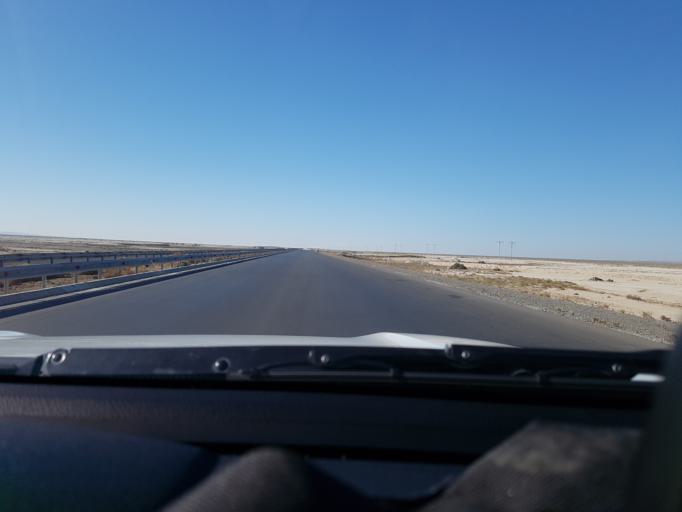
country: TM
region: Balkan
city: Gazanjyk
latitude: 39.2621
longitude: 55.1151
